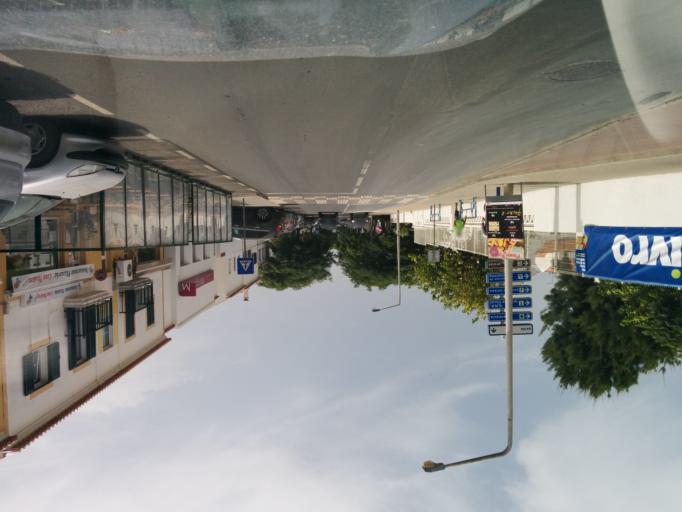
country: PT
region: Beja
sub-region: Odemira
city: Vila Nova de Milfontes
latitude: 37.7260
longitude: -8.7802
